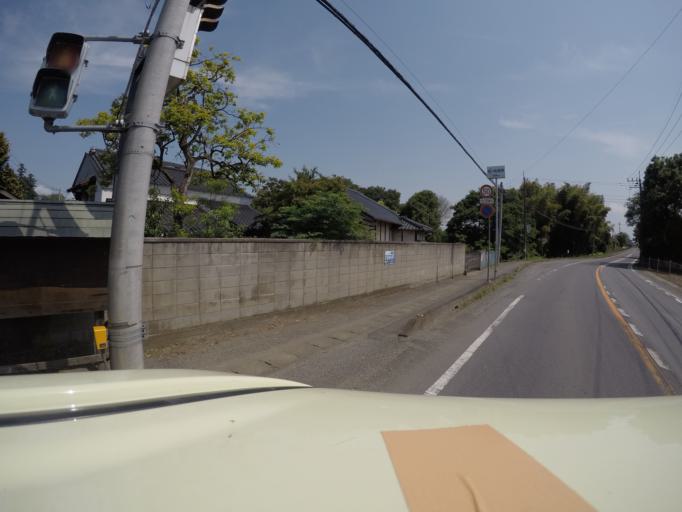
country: JP
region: Ibaraki
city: Mitsukaido
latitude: 36.0435
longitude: 139.9741
